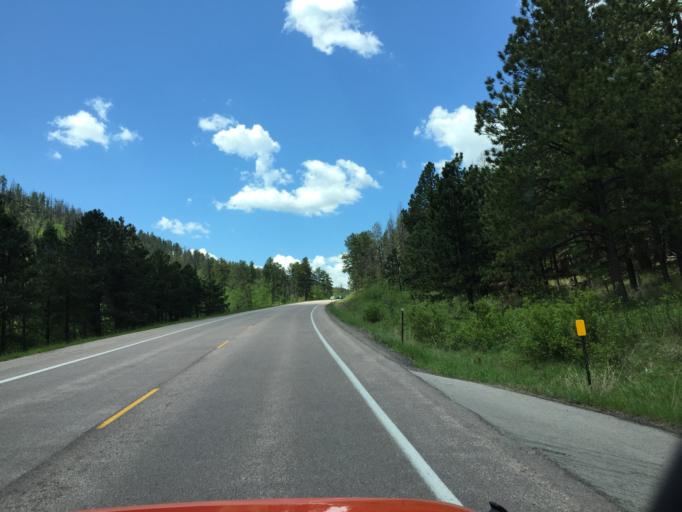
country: US
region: South Dakota
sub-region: Custer County
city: Custer
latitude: 43.8946
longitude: -103.5604
